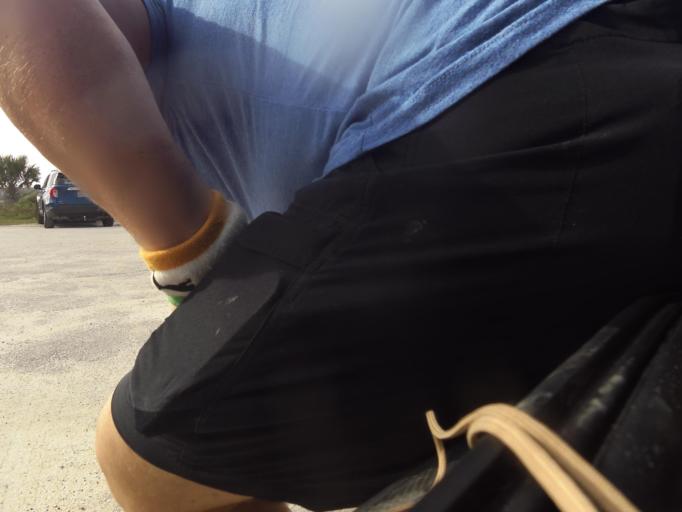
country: US
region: Florida
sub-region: Flagler County
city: Palm Coast
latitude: 29.6362
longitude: -81.1994
